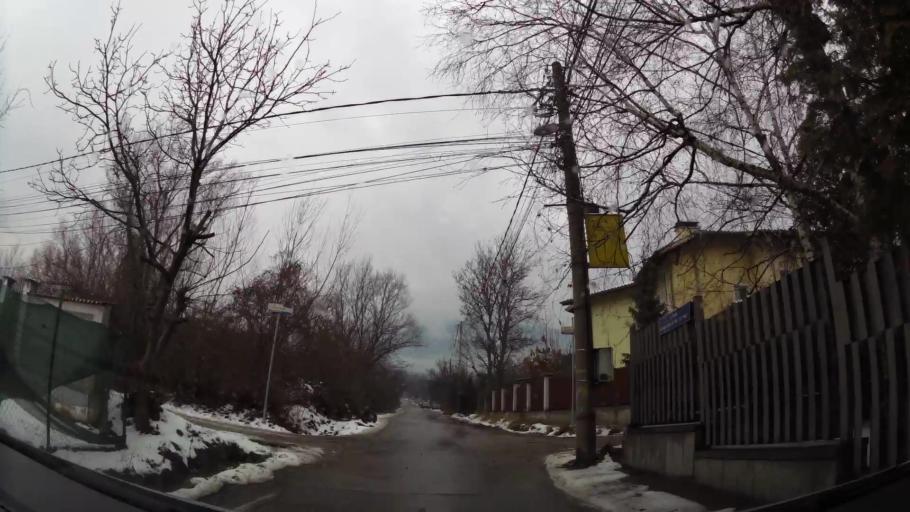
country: BG
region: Sofia-Capital
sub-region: Stolichna Obshtina
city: Sofia
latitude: 42.6508
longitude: 23.2969
